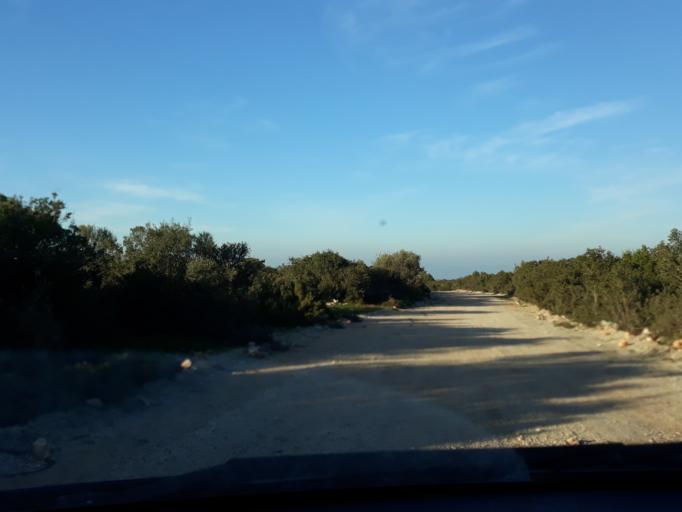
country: GR
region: Central Greece
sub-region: Nomos Voiotias
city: Ayios Thomas
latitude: 38.2425
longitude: 23.5341
